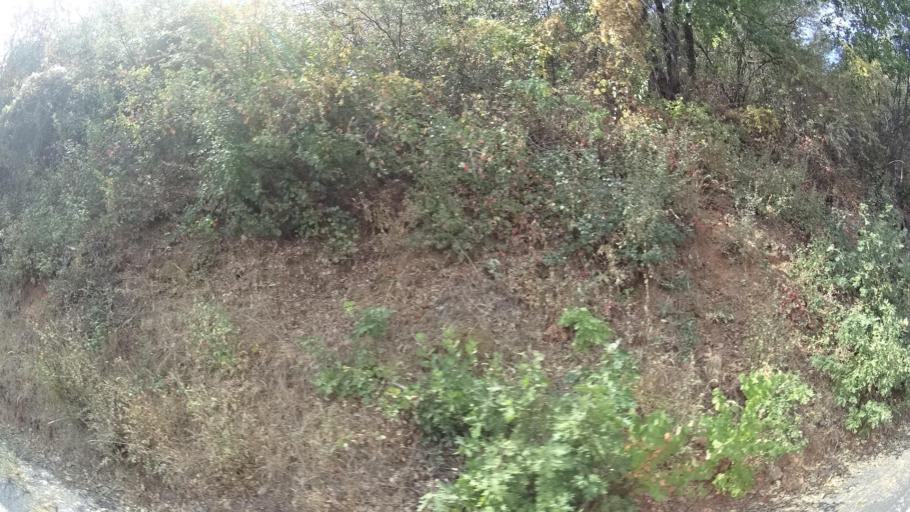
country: US
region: California
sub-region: Mariposa County
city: Midpines
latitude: 37.5607
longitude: -120.0029
